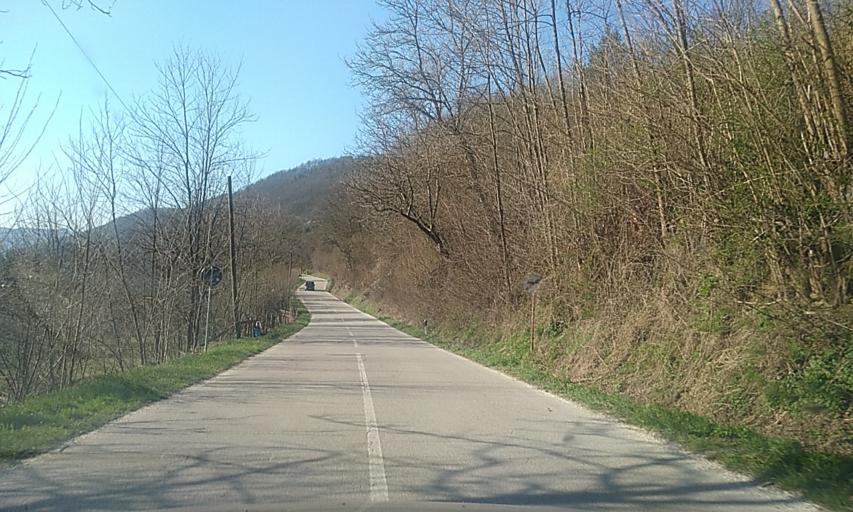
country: RS
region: Central Serbia
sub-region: Pcinjski Okrug
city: Bosilegrad
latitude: 42.4722
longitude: 22.4815
